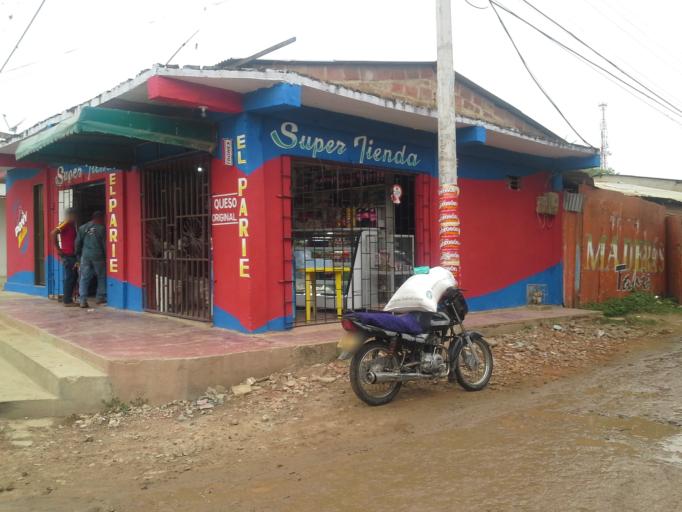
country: CO
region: Bolivar
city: El Carmen de Bolivar
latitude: 9.7179
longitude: -75.1206
